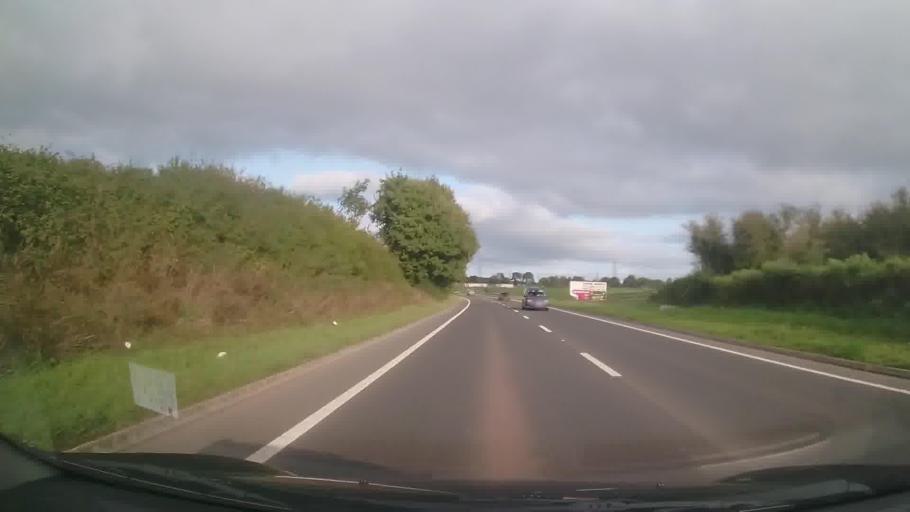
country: GB
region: Wales
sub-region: Pembrokeshire
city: Manorbier
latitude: 51.6925
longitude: -4.8181
